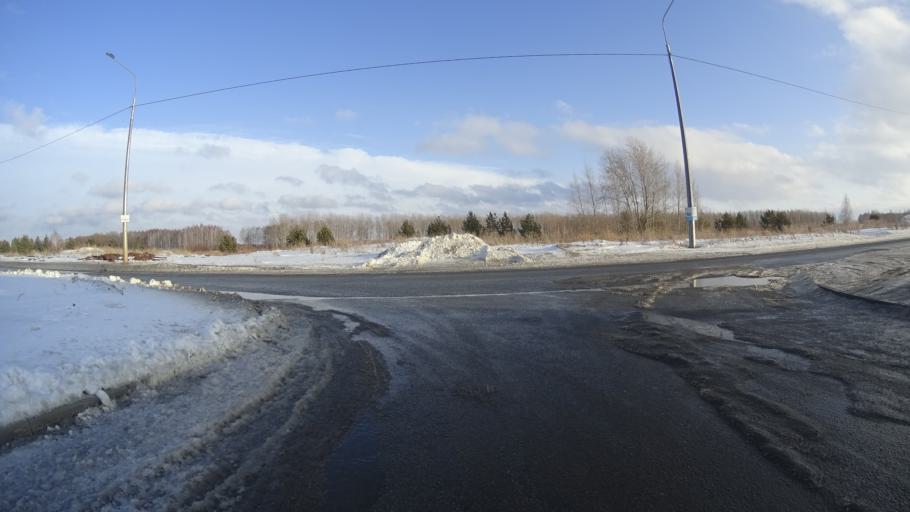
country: RU
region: Chelyabinsk
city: Sargazy
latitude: 55.1027
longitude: 61.2586
